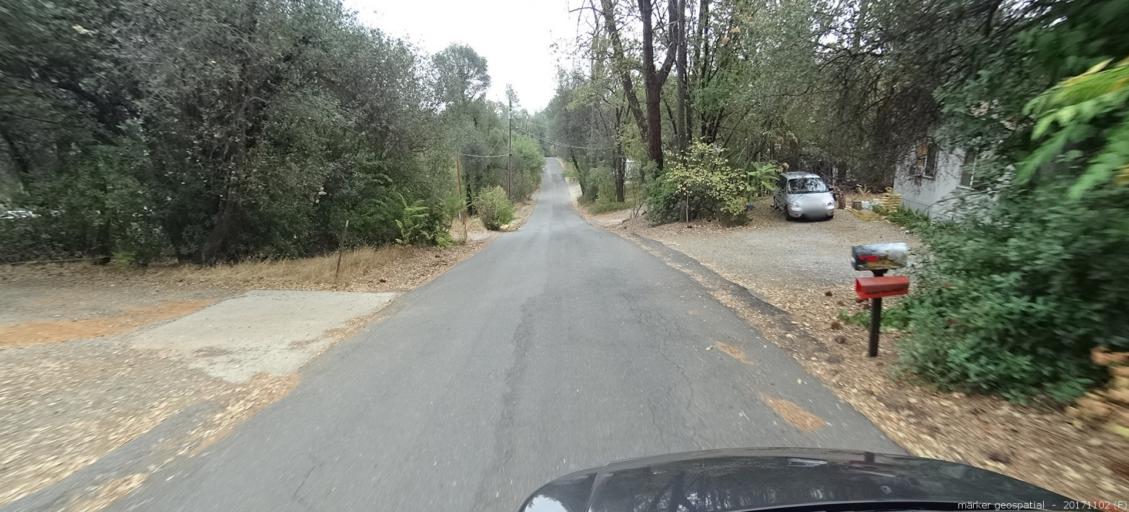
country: US
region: California
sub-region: Shasta County
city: Central Valley (historical)
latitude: 40.6431
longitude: -122.4003
